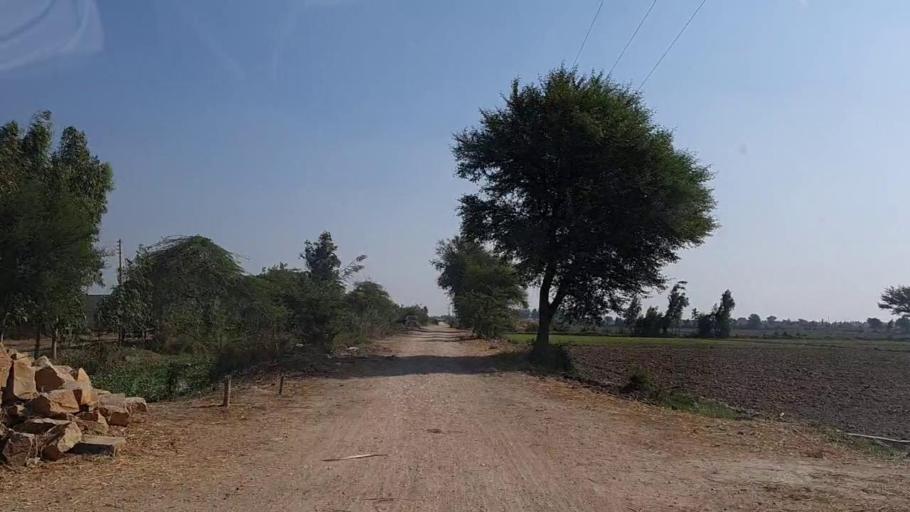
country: PK
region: Sindh
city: Thatta
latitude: 24.7976
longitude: 67.9730
